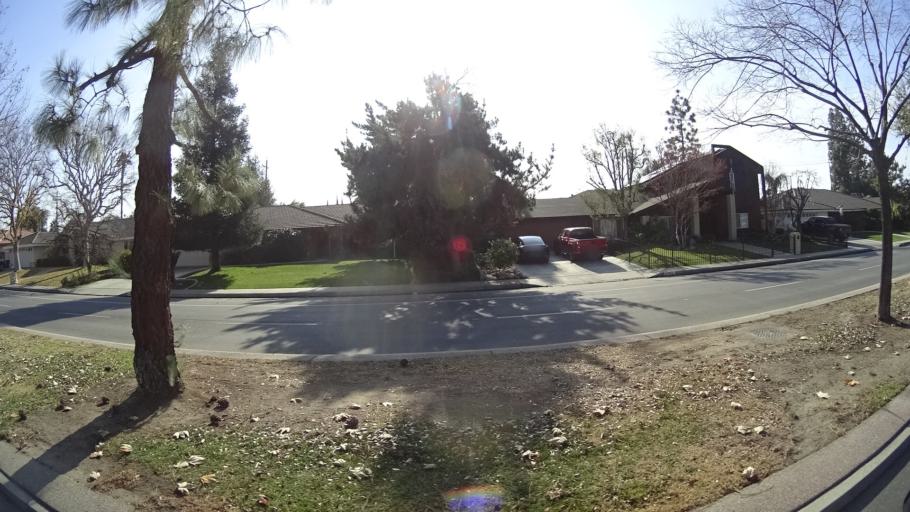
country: US
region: California
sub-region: Kern County
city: Oildale
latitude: 35.4118
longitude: -118.9561
